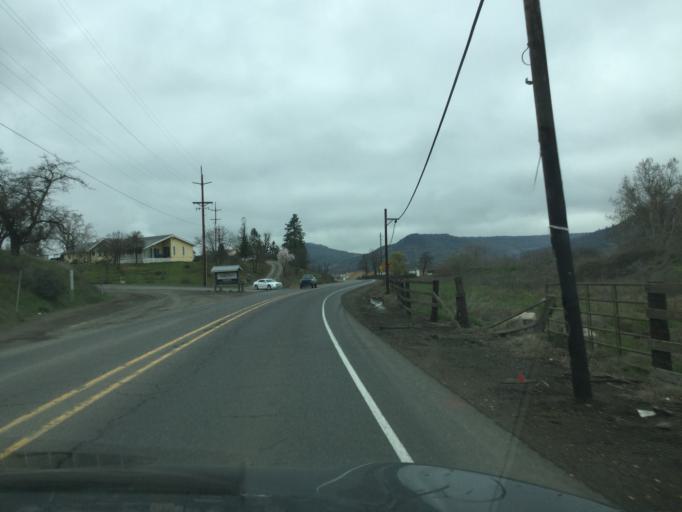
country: US
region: Oregon
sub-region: Jackson County
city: Central Point
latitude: 42.4167
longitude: -122.9517
